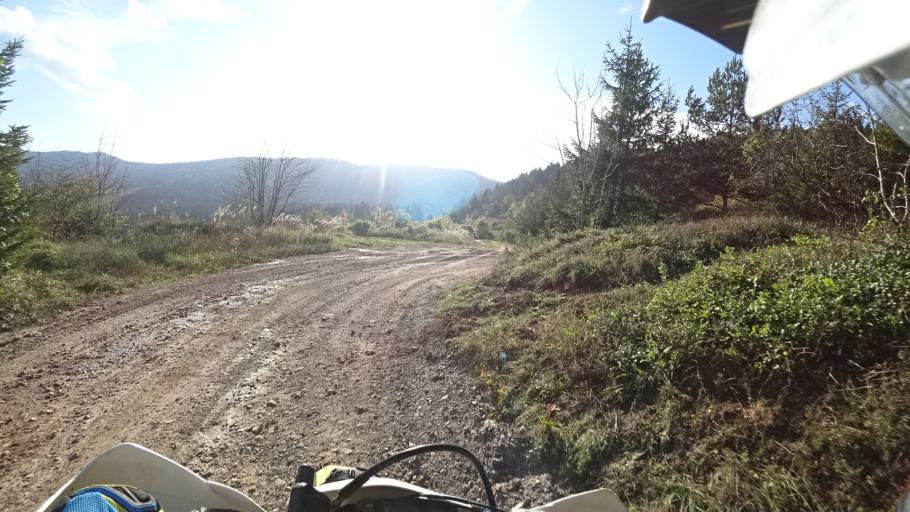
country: HR
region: Licko-Senjska
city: Jezerce
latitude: 44.9282
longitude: 15.4634
